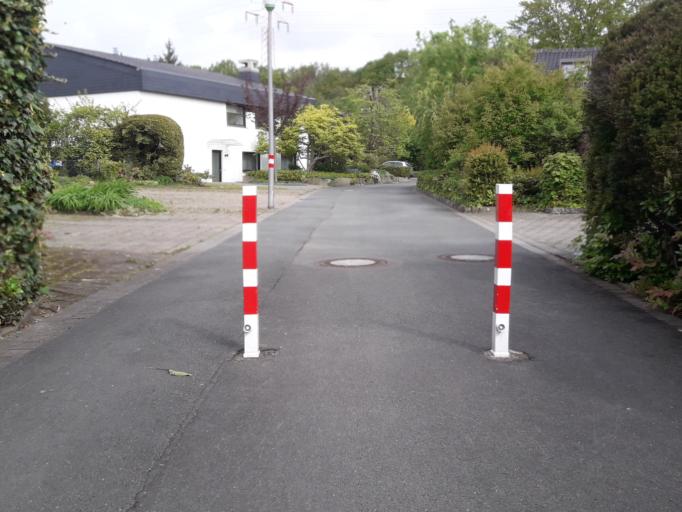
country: DE
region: North Rhine-Westphalia
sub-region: Regierungsbezirk Munster
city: Muenster
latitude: 51.9120
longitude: 7.6542
